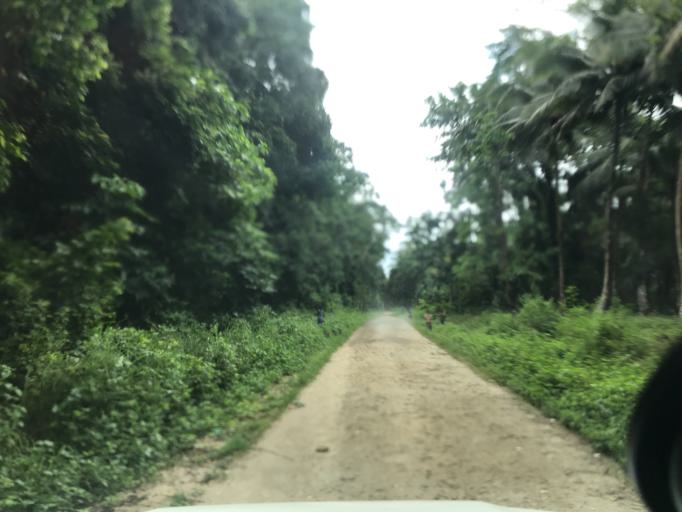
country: VU
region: Sanma
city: Port-Olry
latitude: -15.1685
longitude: 166.9490
